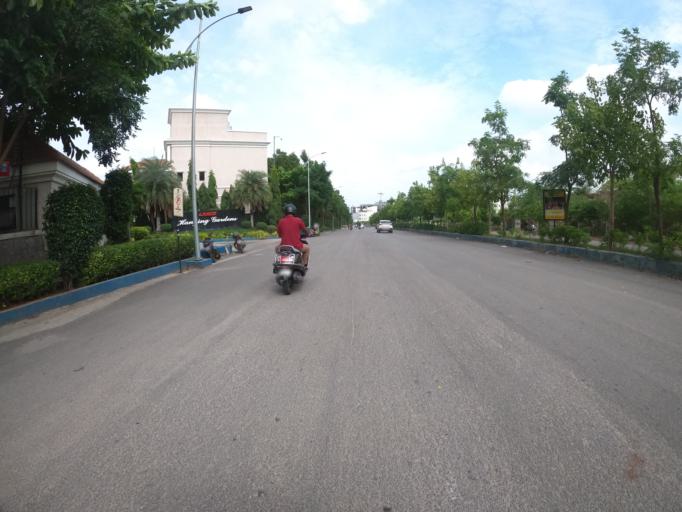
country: IN
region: Telangana
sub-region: Rangareddi
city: Kukatpalli
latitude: 17.4084
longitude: 78.3733
